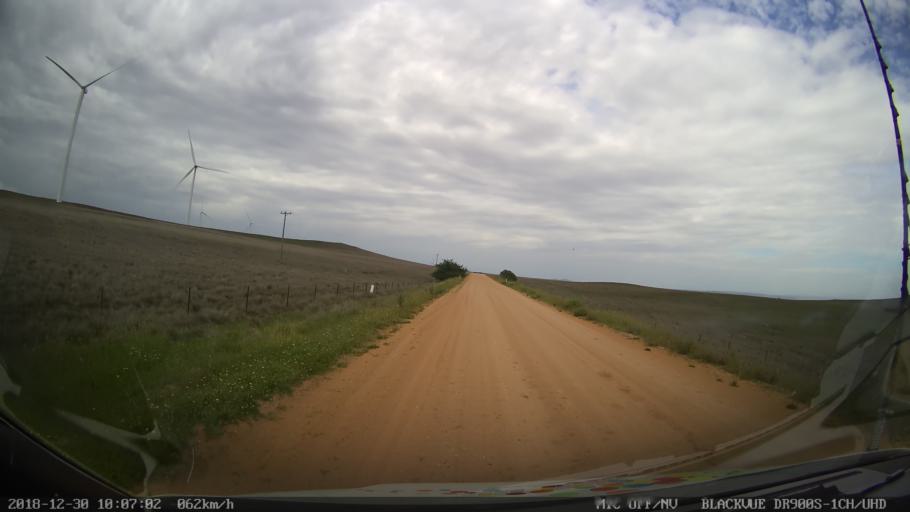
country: AU
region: New South Wales
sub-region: Cooma-Monaro
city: Cooma
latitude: -36.5366
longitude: 149.1256
